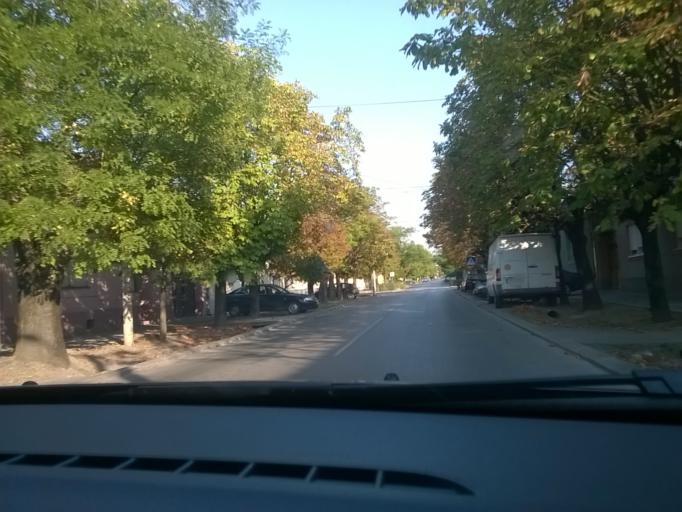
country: RS
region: Autonomna Pokrajina Vojvodina
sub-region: Juznobanatski Okrug
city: Vrsac
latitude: 45.1146
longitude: 21.3007
